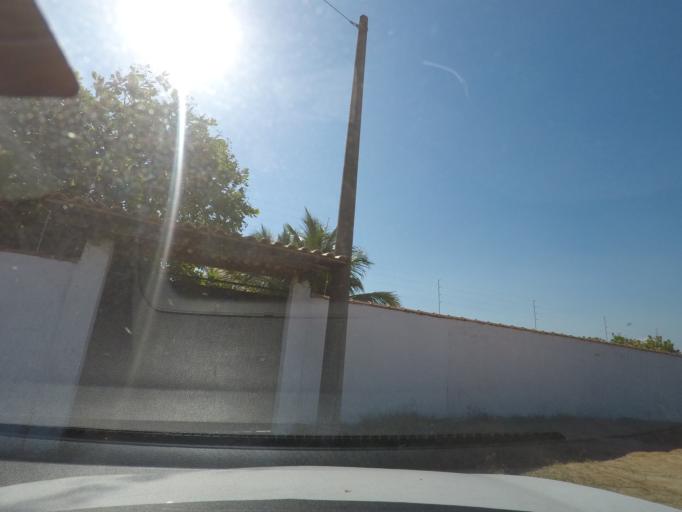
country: BR
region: Rio de Janeiro
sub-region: Marica
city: Marica
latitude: -22.9648
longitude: -42.9038
